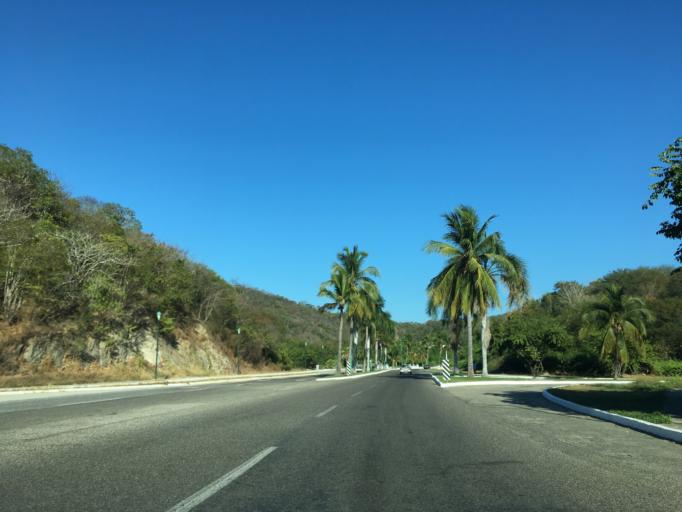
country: MX
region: Oaxaca
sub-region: Santa Maria Huatulco
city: Crucecita
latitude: 15.7665
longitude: -96.1212
